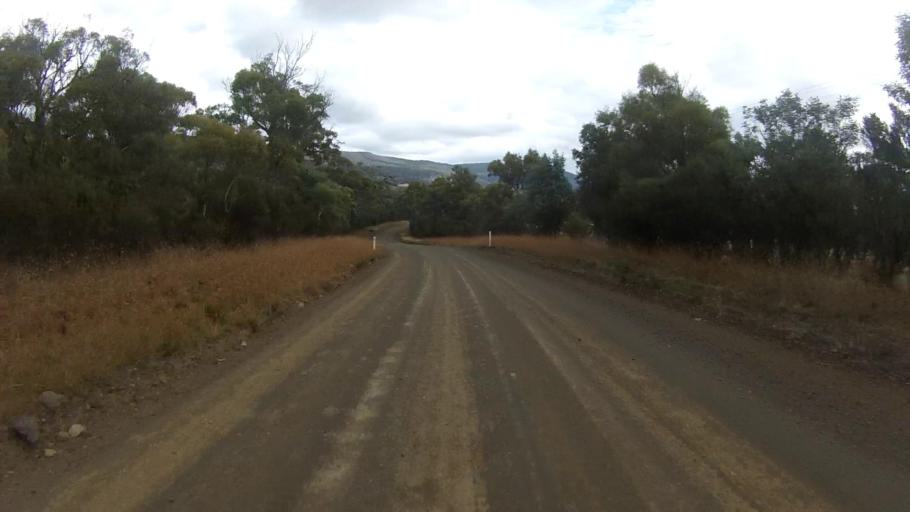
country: AU
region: Tasmania
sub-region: Break O'Day
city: St Helens
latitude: -41.8208
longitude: 147.9903
